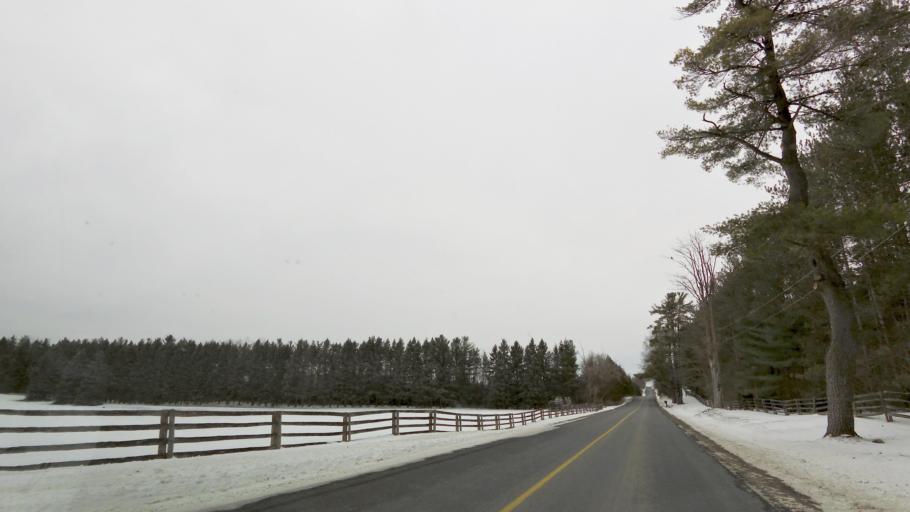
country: CA
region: Ontario
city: Bradford West Gwillimbury
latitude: 43.9480
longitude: -79.6379
